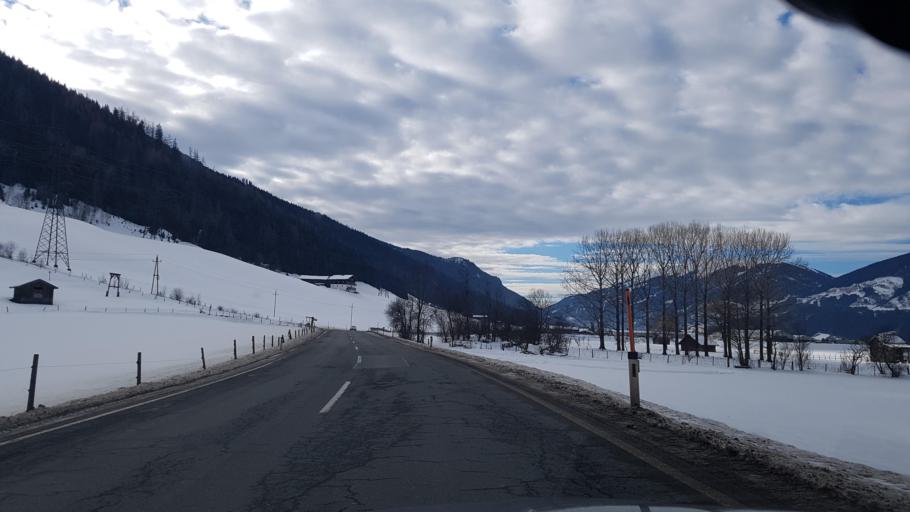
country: AT
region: Salzburg
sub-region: Politischer Bezirk Zell am See
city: Mittersill
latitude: 47.2779
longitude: 12.4632
